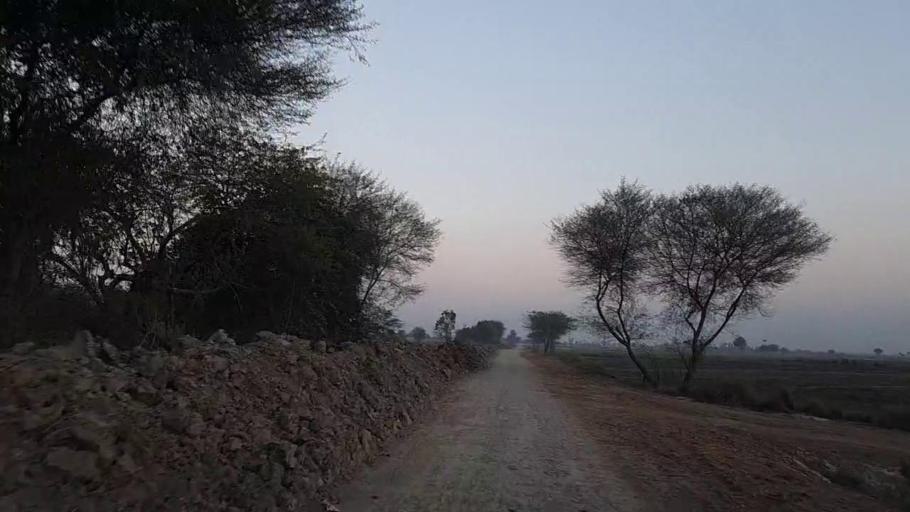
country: PK
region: Sindh
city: Naushahro Firoz
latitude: 26.7960
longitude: 68.0369
